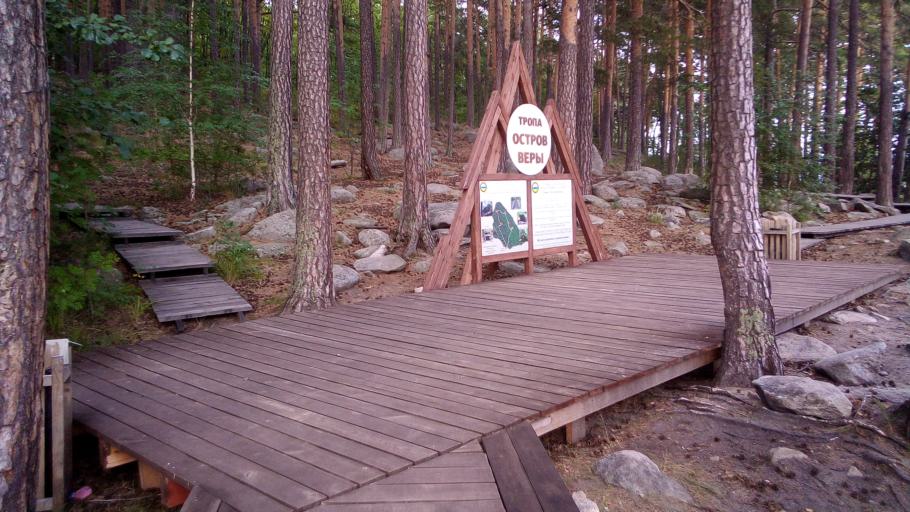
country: RU
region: Chelyabinsk
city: Turgoyak
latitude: 55.1600
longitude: 60.0316
